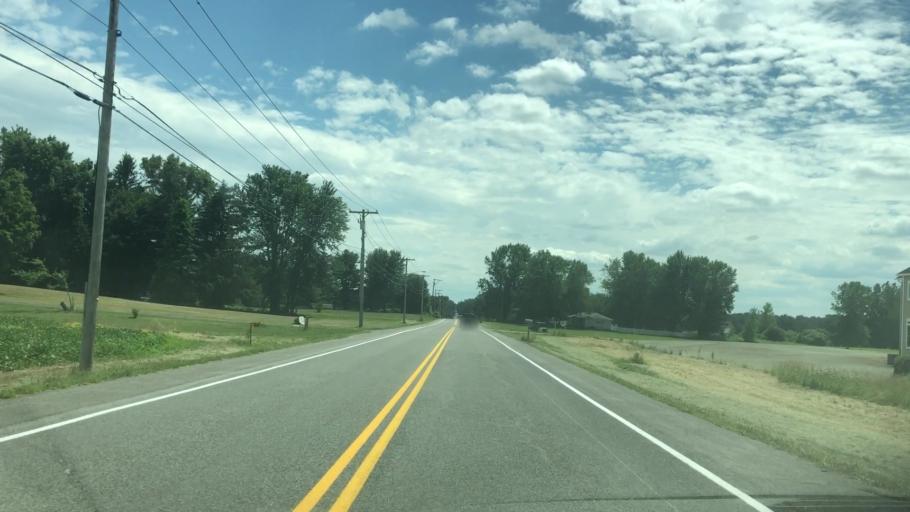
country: US
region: New York
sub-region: Monroe County
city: Webster
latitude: 43.1562
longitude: -77.4006
